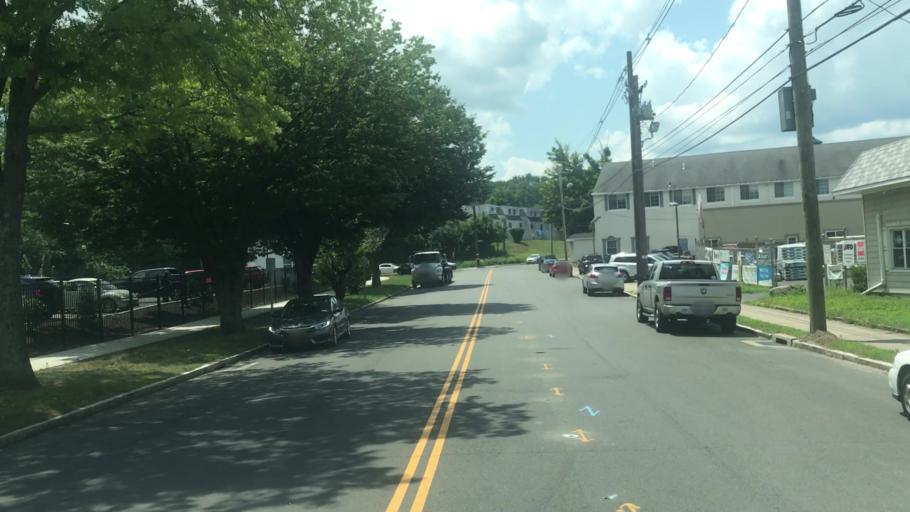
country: US
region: Connecticut
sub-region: Fairfield County
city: Danbury
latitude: 41.3981
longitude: -73.4593
